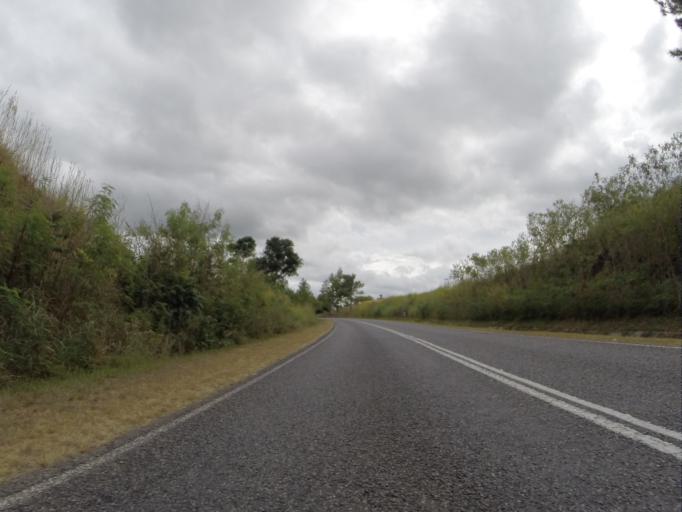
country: FJ
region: Western
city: Nadi
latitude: -18.0230
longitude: 177.3307
